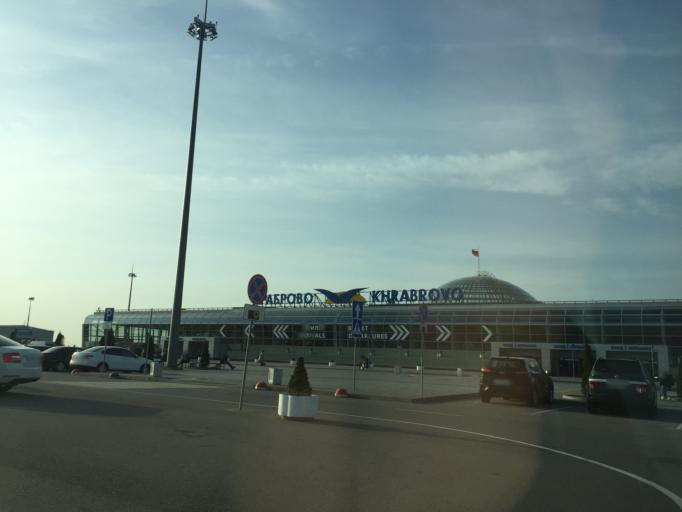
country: RU
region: Kaliningrad
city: Gur'yevsk
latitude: 54.8821
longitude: 20.5873
